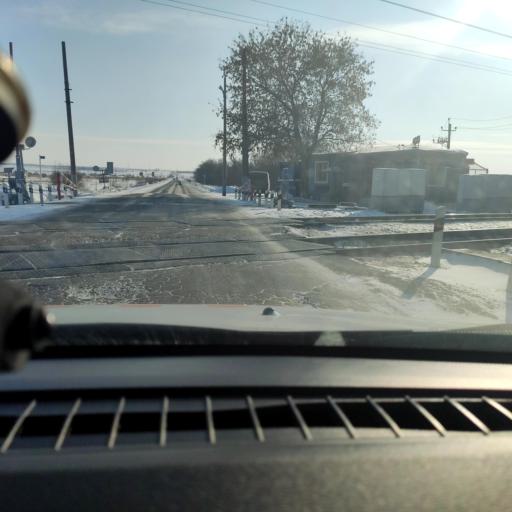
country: RU
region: Samara
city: Smyshlyayevka
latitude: 53.1708
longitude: 50.4571
